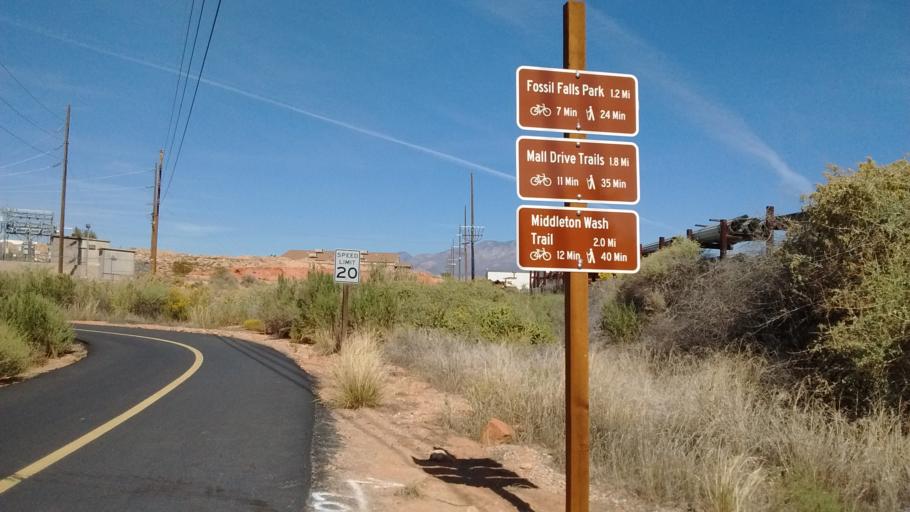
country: US
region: Utah
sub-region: Washington County
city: Washington
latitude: 37.1123
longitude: -113.5138
